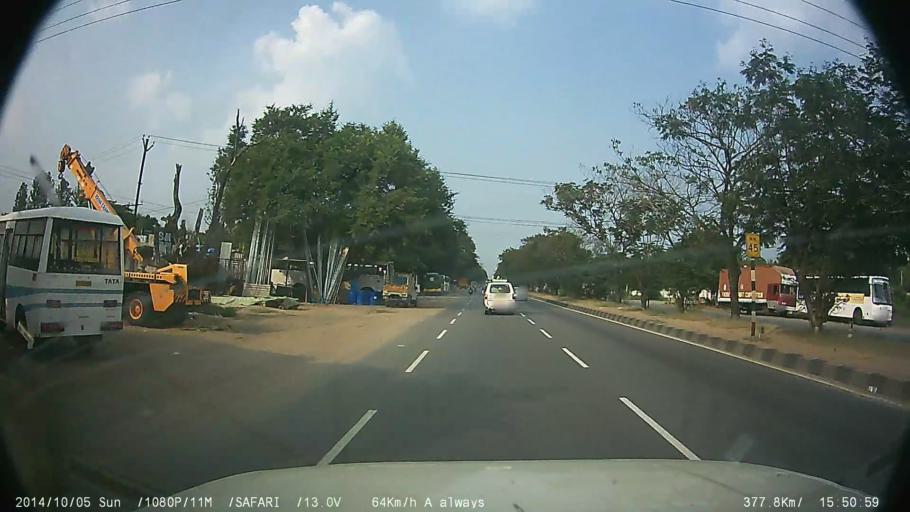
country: IN
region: Tamil Nadu
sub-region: Kancheepuram
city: Singapperumalkovil
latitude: 12.7870
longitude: 80.0151
